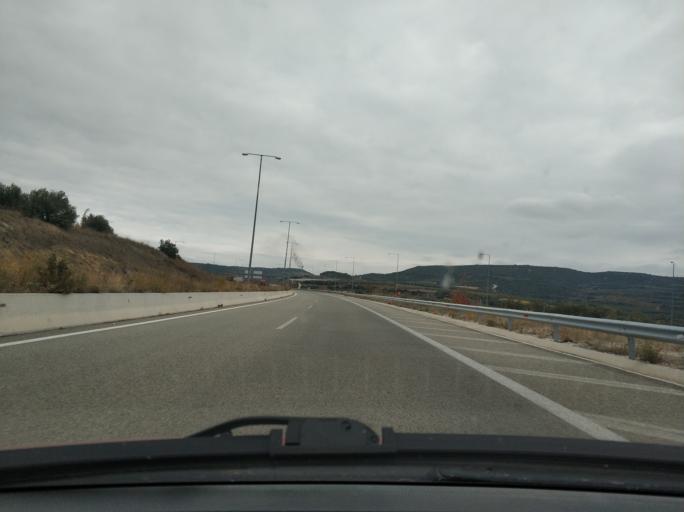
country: GR
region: East Macedonia and Thrace
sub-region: Nomos Kavalas
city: Paralia Ofryniou
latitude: 40.7856
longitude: 23.9580
